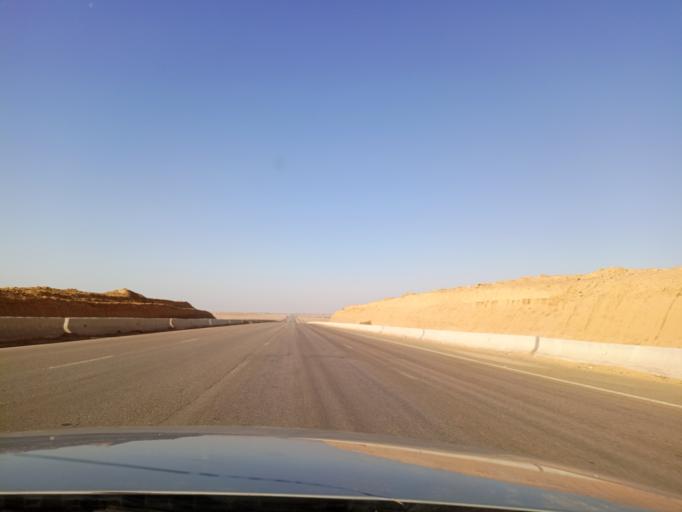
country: EG
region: Muhafazat al Fayyum
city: Tamiyah
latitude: 29.6162
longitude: 30.9337
